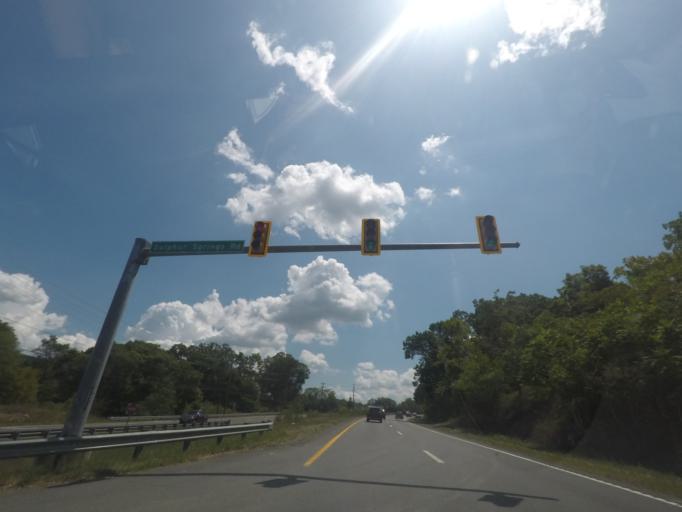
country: US
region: Virginia
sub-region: City of Winchester
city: Winchester
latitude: 39.1498
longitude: -78.1316
